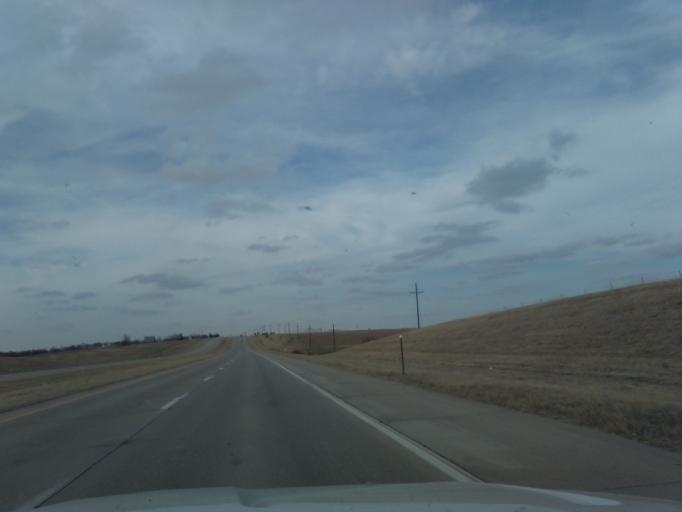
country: US
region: Nebraska
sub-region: Gage County
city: Beatrice
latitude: 40.3290
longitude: -96.7466
